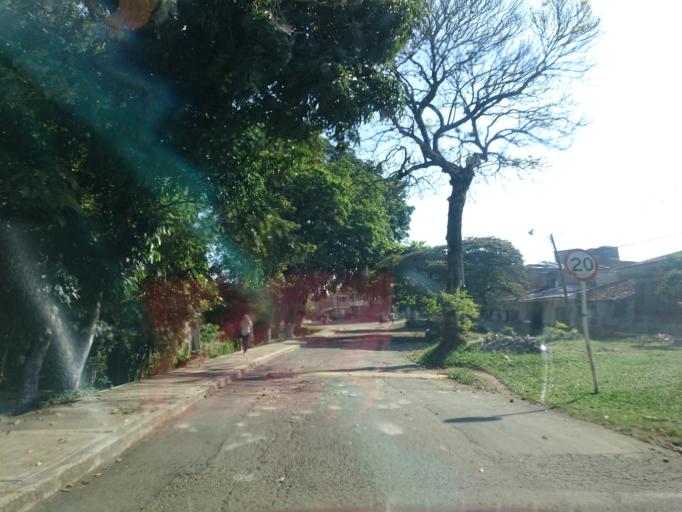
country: CO
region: Cauca
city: Santander de Quilichao
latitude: 3.0075
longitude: -76.4807
